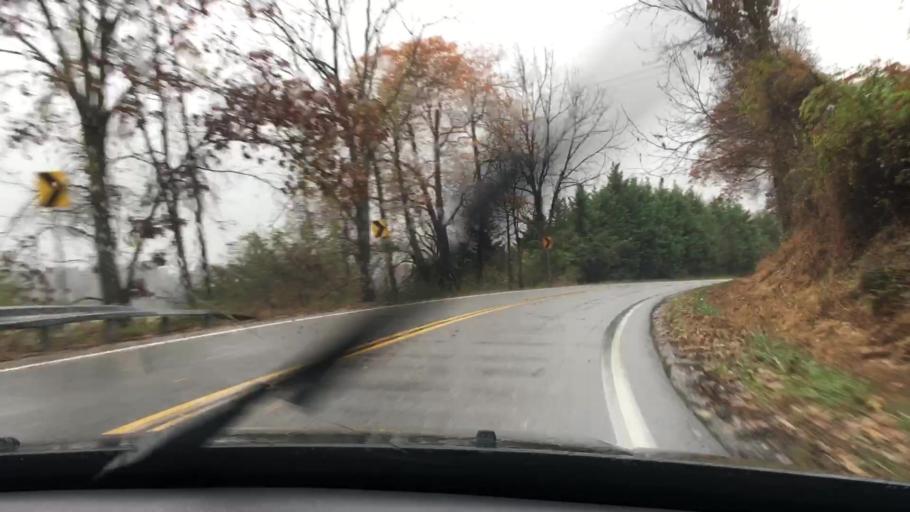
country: US
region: Pennsylvania
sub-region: York County
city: Glen Rock
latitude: 39.7717
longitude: -76.7307
